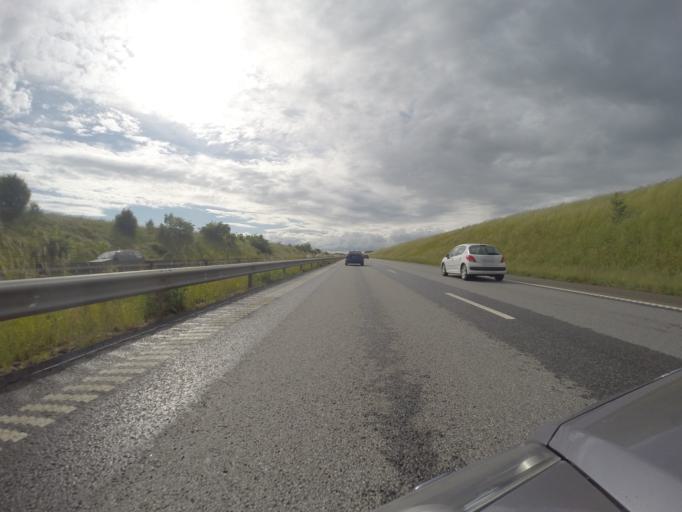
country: SE
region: Skane
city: Bjarred
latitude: 55.7370
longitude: 13.0616
